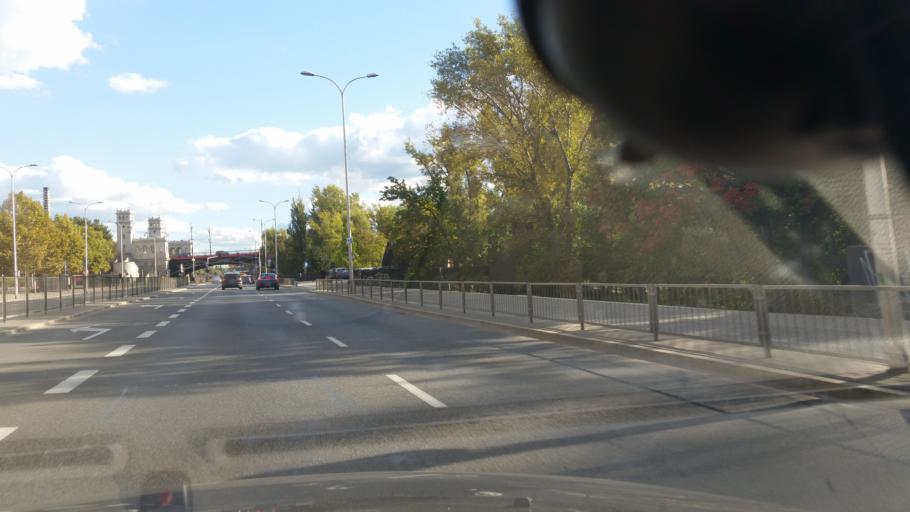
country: PL
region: Masovian Voivodeship
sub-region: Warszawa
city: Praga Polnoc
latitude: 52.2388
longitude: 21.0426
